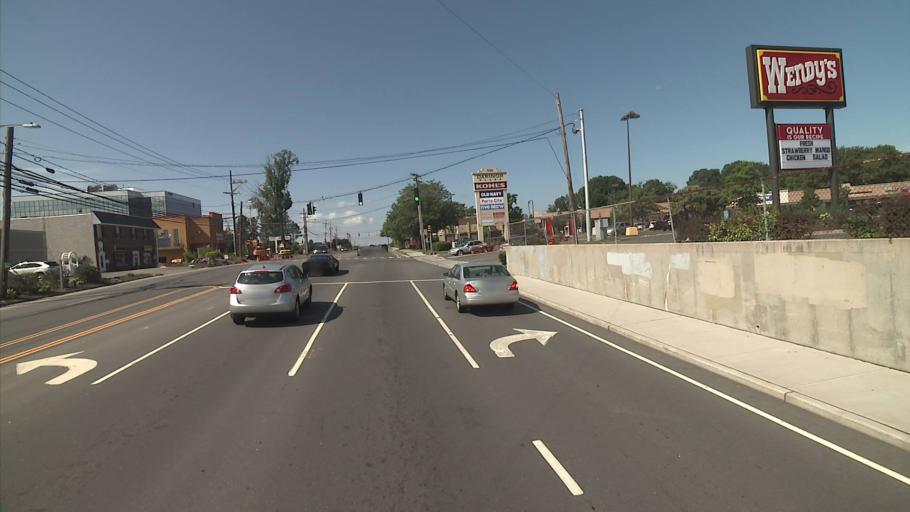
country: US
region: Connecticut
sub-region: Fairfield County
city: Darien
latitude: 41.0988
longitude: -73.4432
